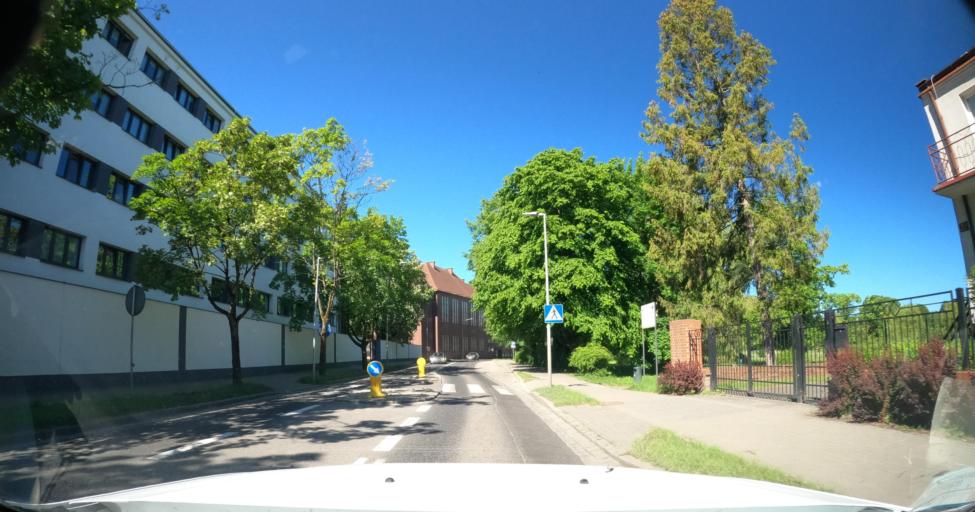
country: PL
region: Pomeranian Voivodeship
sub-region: Slupsk
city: Slupsk
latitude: 54.4728
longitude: 17.0333
